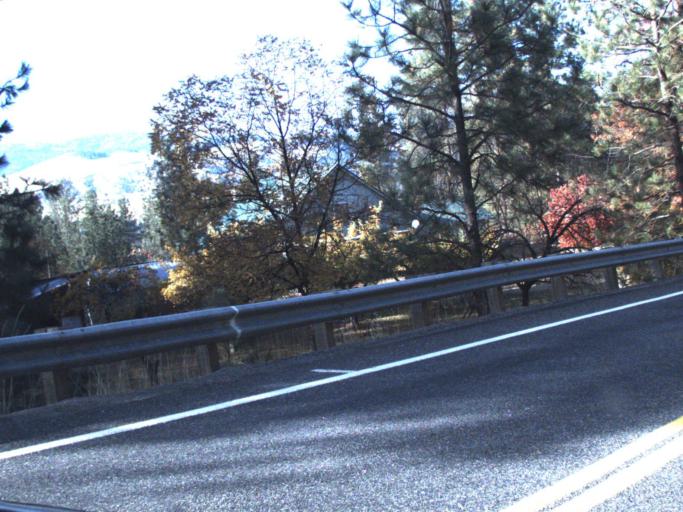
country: US
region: Washington
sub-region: Stevens County
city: Kettle Falls
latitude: 48.4828
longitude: -118.1733
